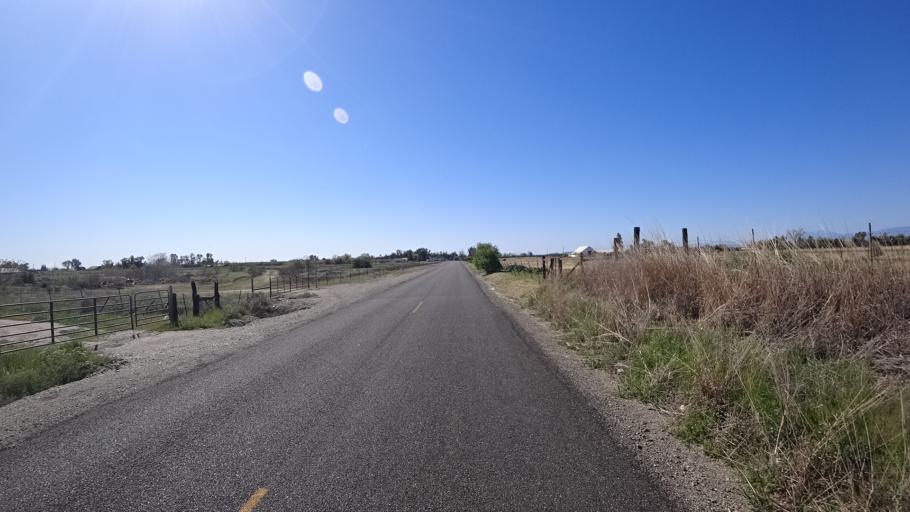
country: US
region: California
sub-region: Glenn County
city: Orland
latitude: 39.7297
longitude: -122.2158
